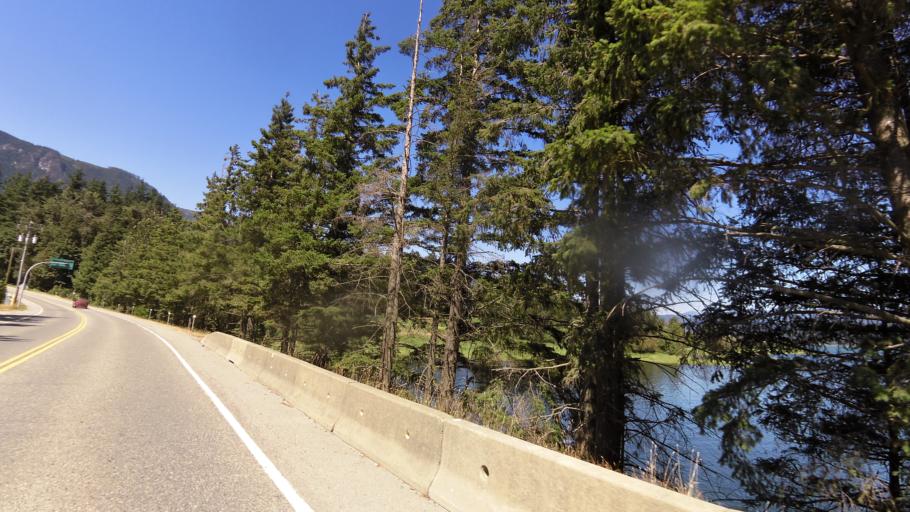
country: CA
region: British Columbia
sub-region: Fraser Valley Regional District
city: Chilliwack
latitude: 49.2488
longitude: -121.9486
